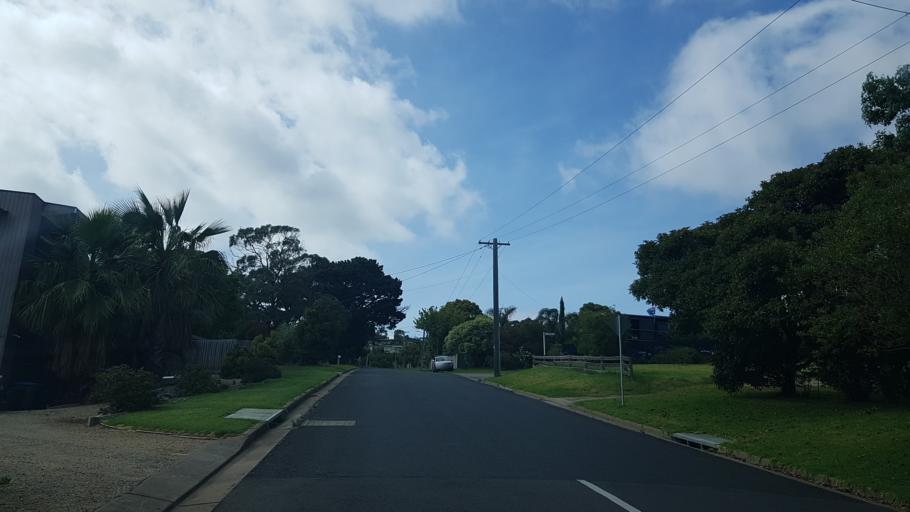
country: AU
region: Victoria
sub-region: Mornington Peninsula
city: Dromana
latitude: -38.3436
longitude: 144.9741
